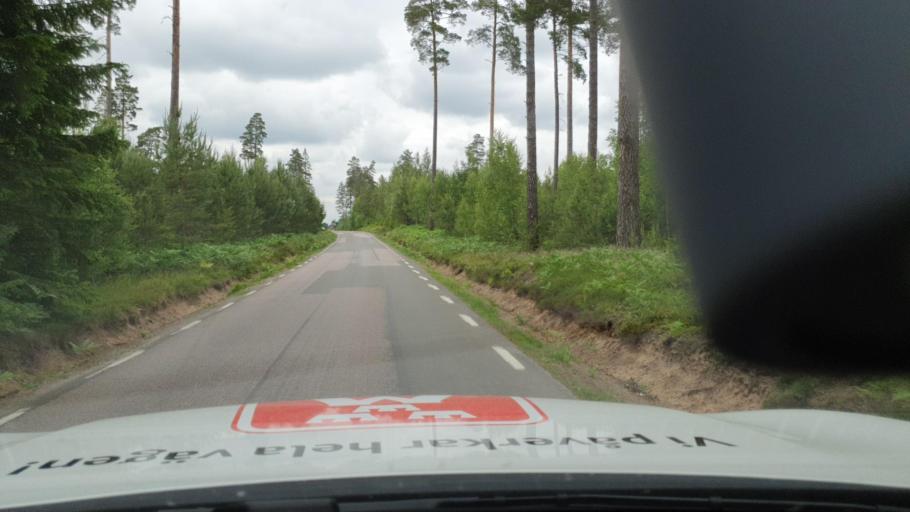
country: SE
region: Vaestra Goetaland
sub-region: Tidaholms Kommun
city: Olofstorp
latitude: 58.2662
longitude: 14.0986
